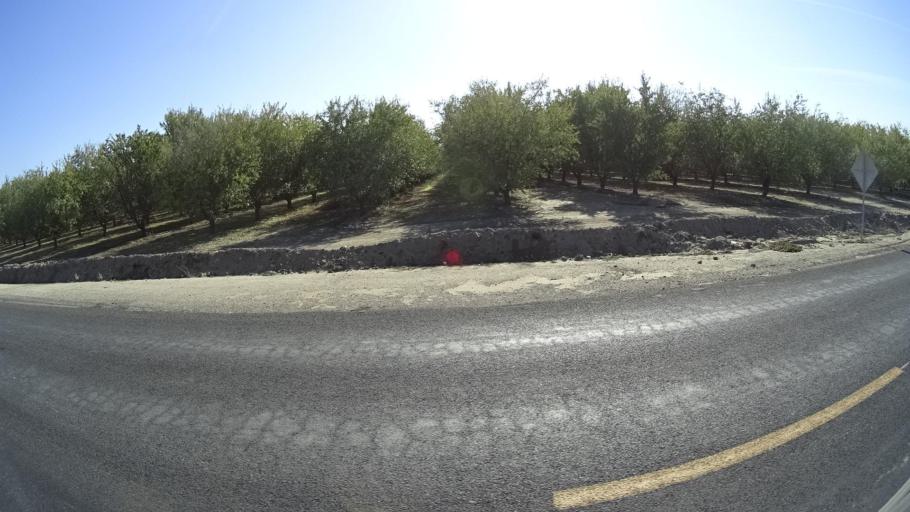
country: US
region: California
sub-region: Kern County
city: McFarland
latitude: 35.6453
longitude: -119.2853
